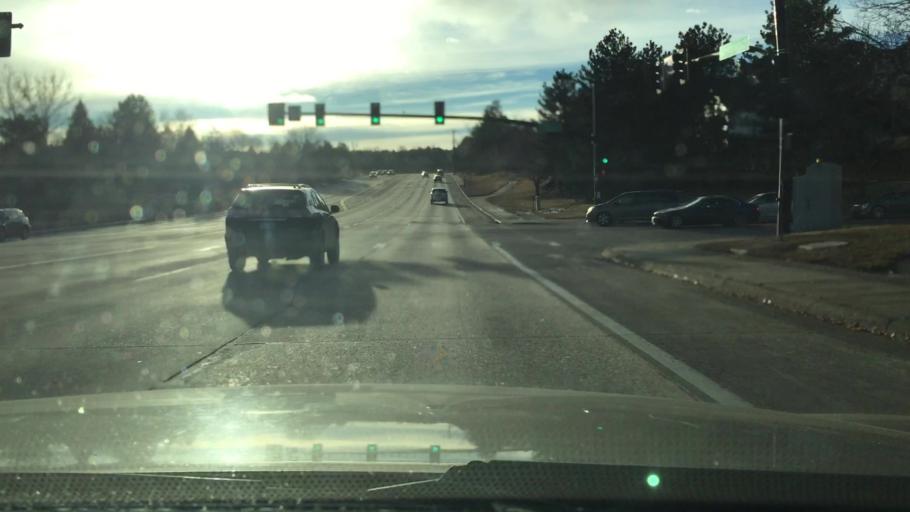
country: US
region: Colorado
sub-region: Douglas County
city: Highlands Ranch
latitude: 39.5441
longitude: -104.9717
